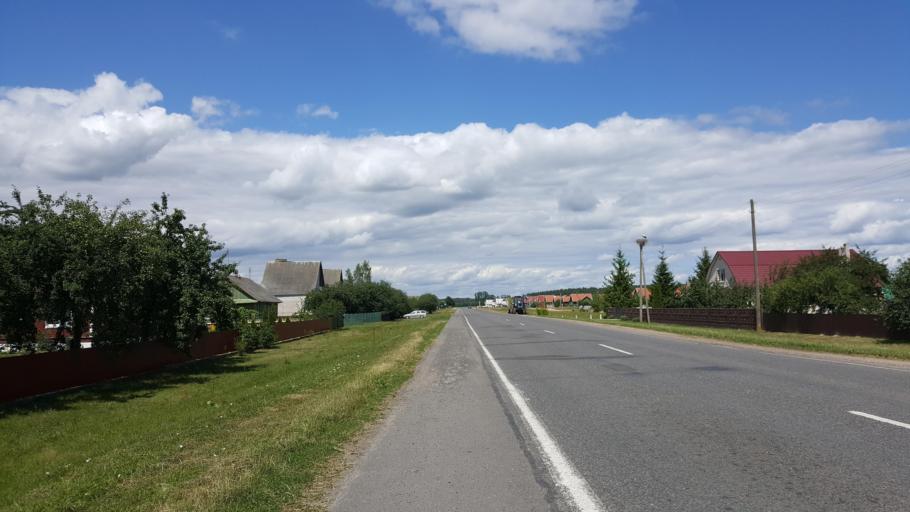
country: BY
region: Brest
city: Kamyanyets
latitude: 52.3230
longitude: 23.9179
